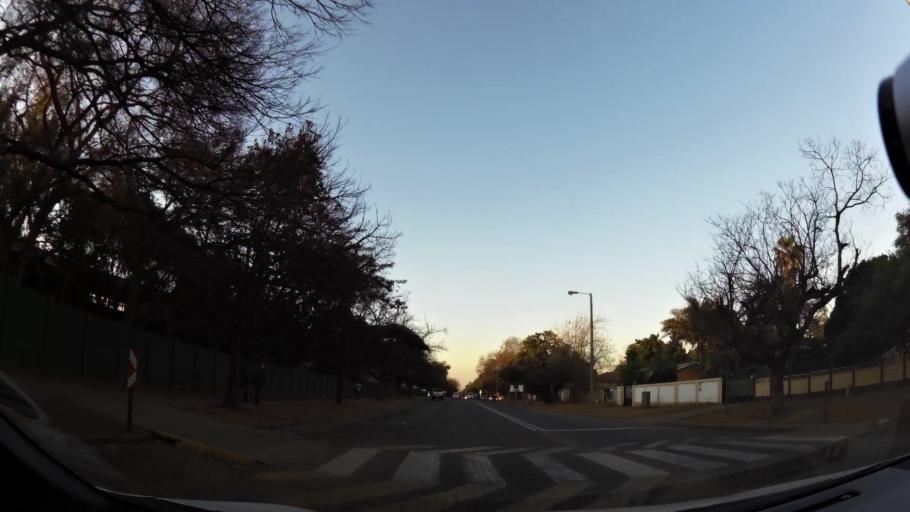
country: ZA
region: North-West
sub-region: Bojanala Platinum District Municipality
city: Rustenburg
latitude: -25.6736
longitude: 27.2254
